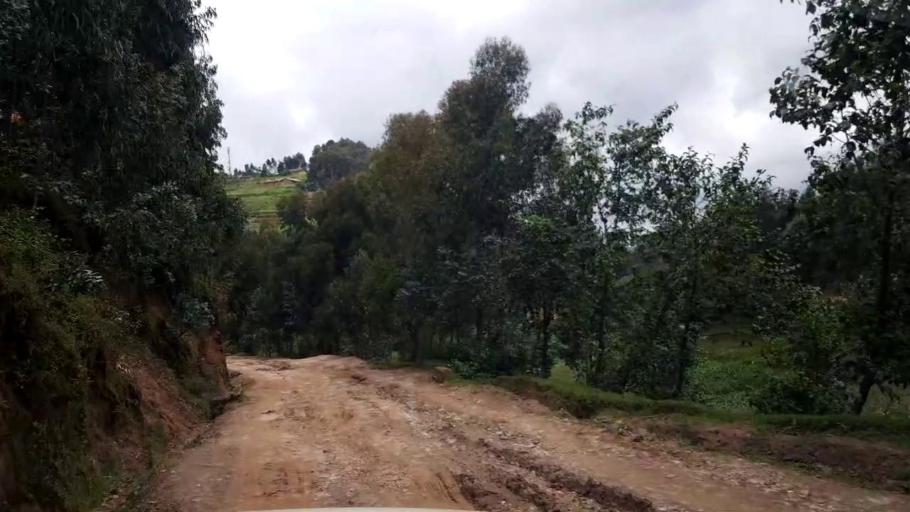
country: RW
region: Western Province
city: Kibuye
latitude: -1.9376
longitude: 29.4458
